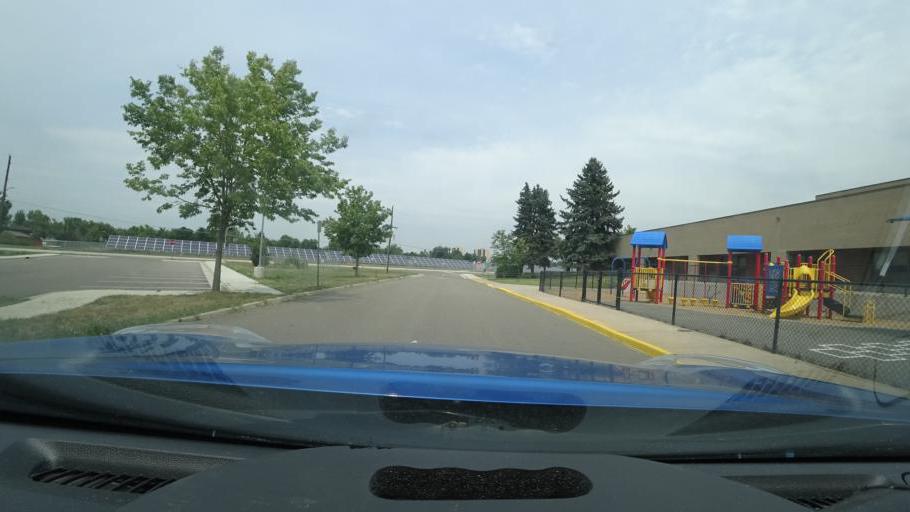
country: US
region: Colorado
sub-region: Arapahoe County
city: Glendale
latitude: 39.6888
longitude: -104.9071
